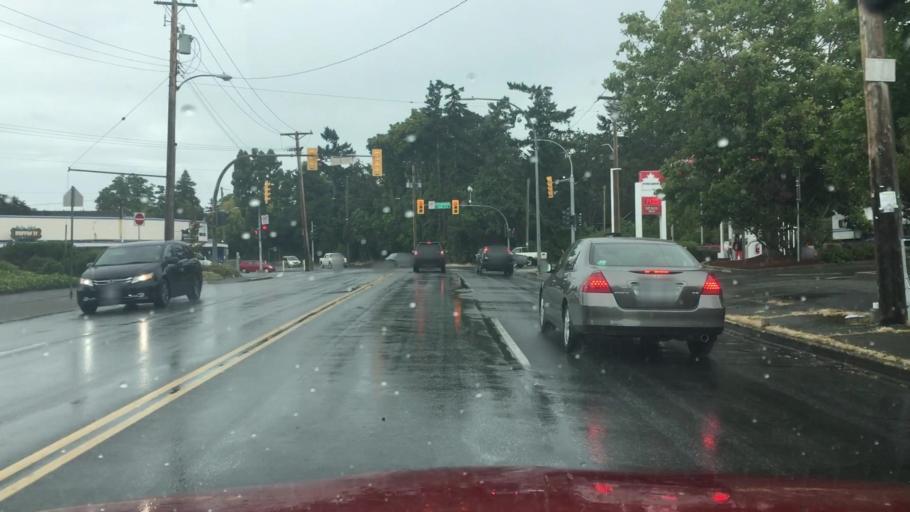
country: CA
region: British Columbia
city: Victoria
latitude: 48.4552
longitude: -123.3596
